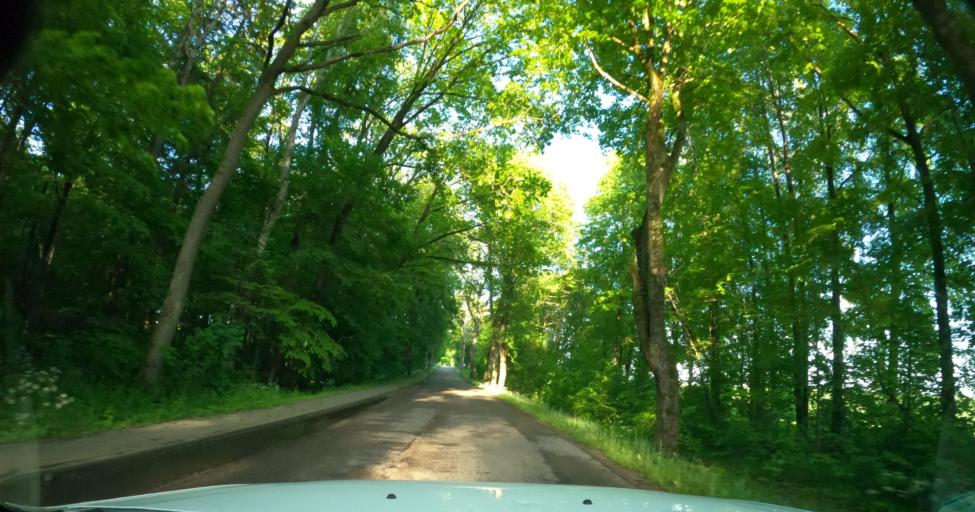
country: PL
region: Warmian-Masurian Voivodeship
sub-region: Powiat braniewski
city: Pieniezno
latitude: 54.2551
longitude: 19.9700
